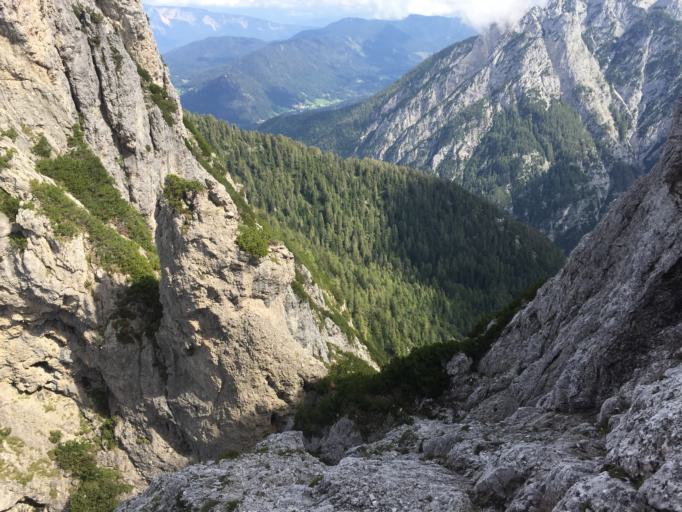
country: IT
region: Friuli Venezia Giulia
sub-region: Provincia di Udine
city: Tarvisio
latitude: 46.4594
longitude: 13.5888
